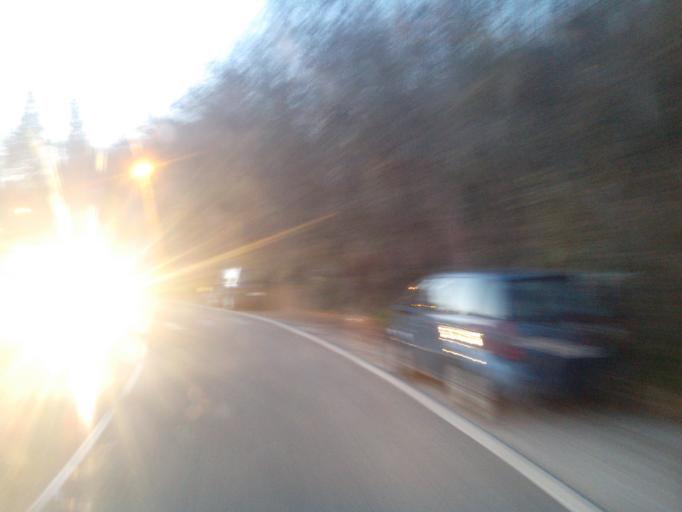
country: FR
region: Midi-Pyrenees
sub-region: Departement de l'Ariege
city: Foix
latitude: 42.9663
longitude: 1.5995
